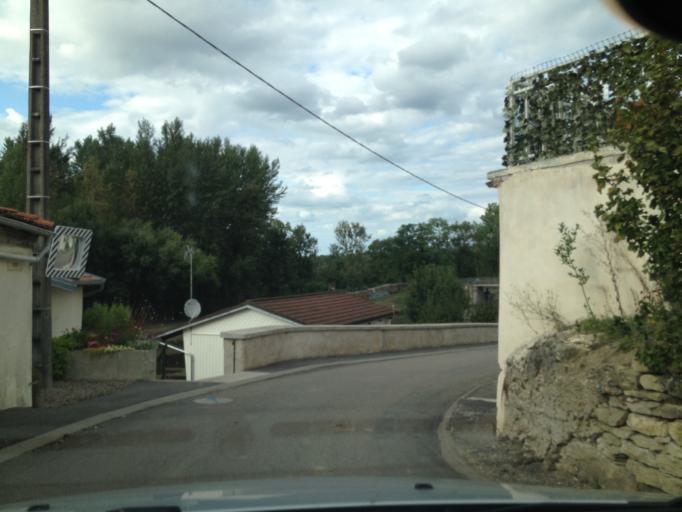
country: FR
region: Franche-Comte
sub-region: Departement de la Haute-Saone
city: Jussey
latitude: 47.8908
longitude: 5.9799
